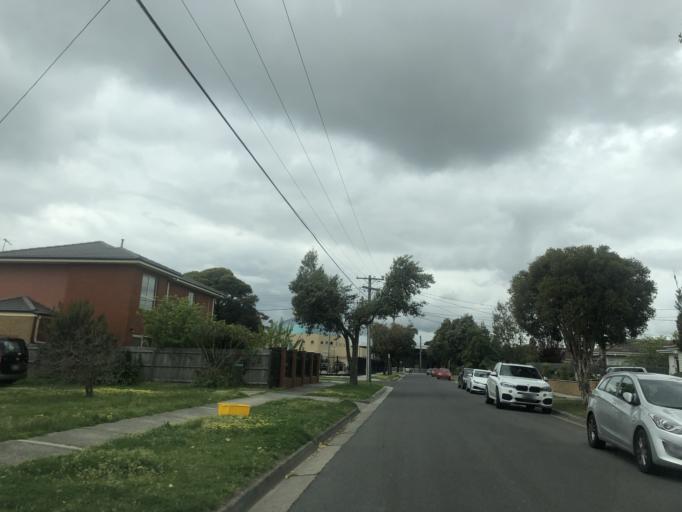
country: AU
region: Victoria
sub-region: Greater Dandenong
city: Dandenong North
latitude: -37.9748
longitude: 145.2146
